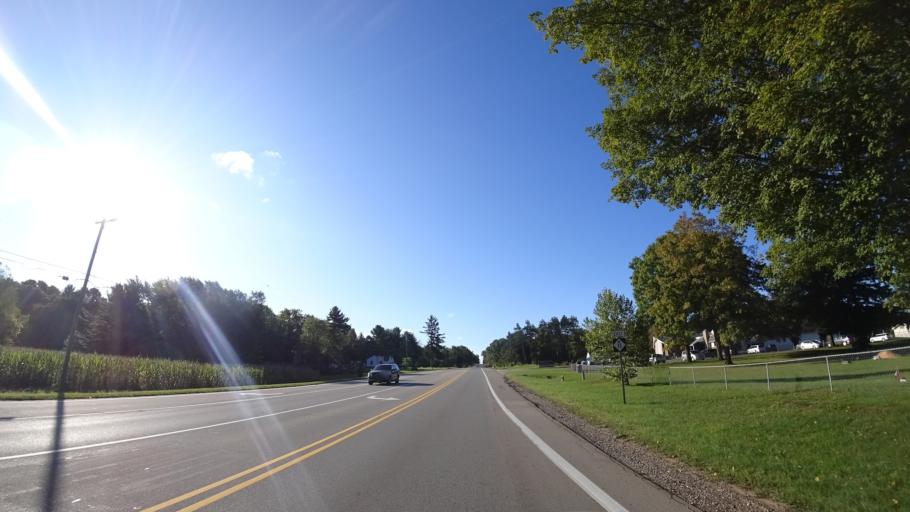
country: US
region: Michigan
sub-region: Kent County
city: Grandville
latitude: 42.9352
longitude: -85.7744
